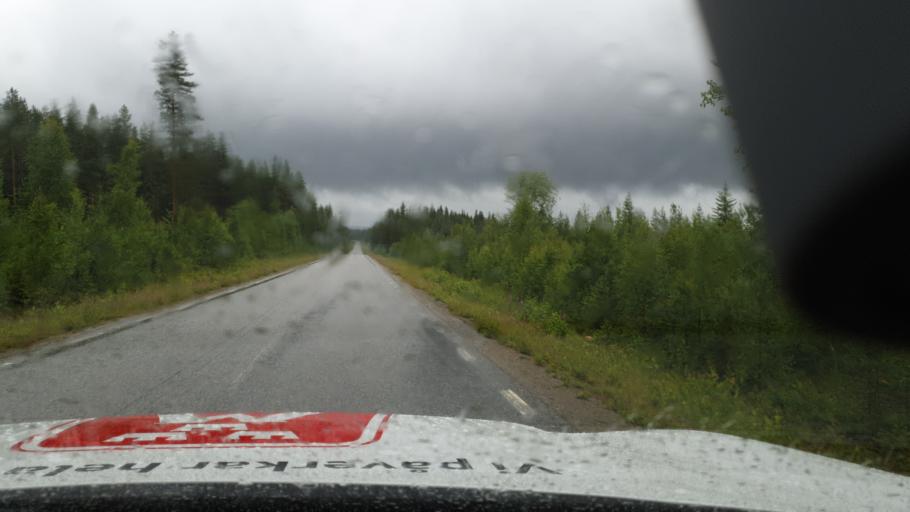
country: SE
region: Vaesterbotten
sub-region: Skelleftea Kommun
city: Langsele
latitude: 64.6246
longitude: 19.9809
